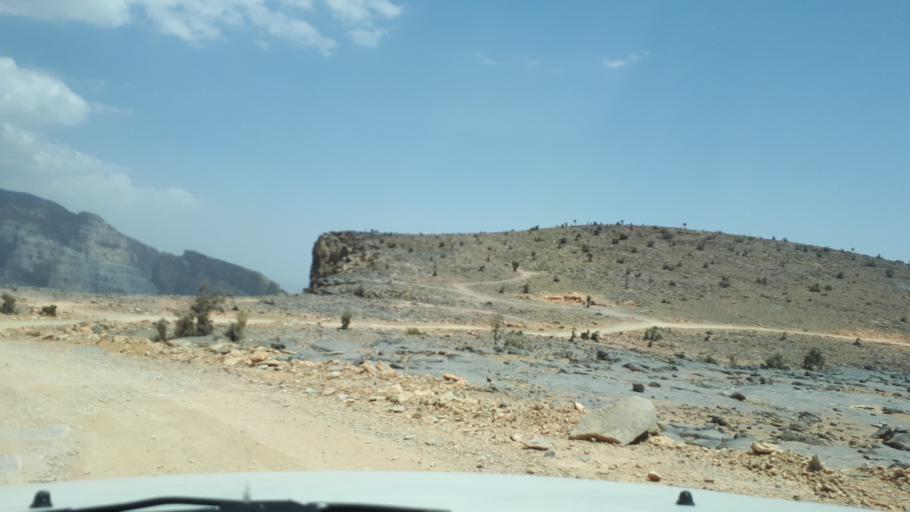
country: OM
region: Muhafazat ad Dakhiliyah
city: Bahla'
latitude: 23.2010
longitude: 57.2005
